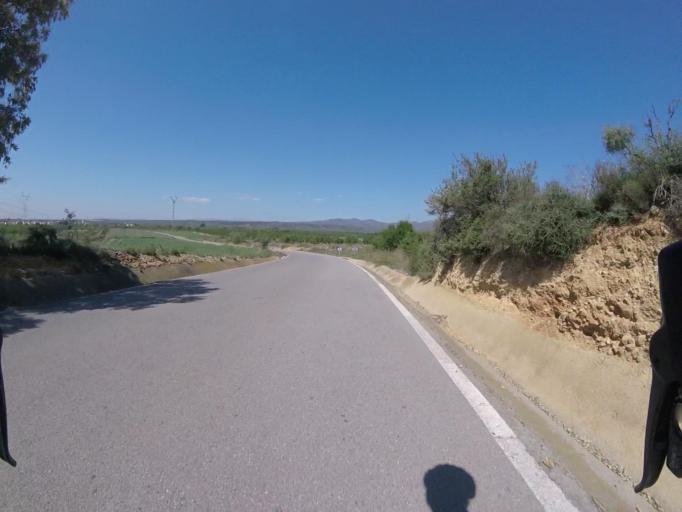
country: ES
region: Valencia
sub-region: Provincia de Castello
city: Benlloch
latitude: 40.2194
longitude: 0.0438
